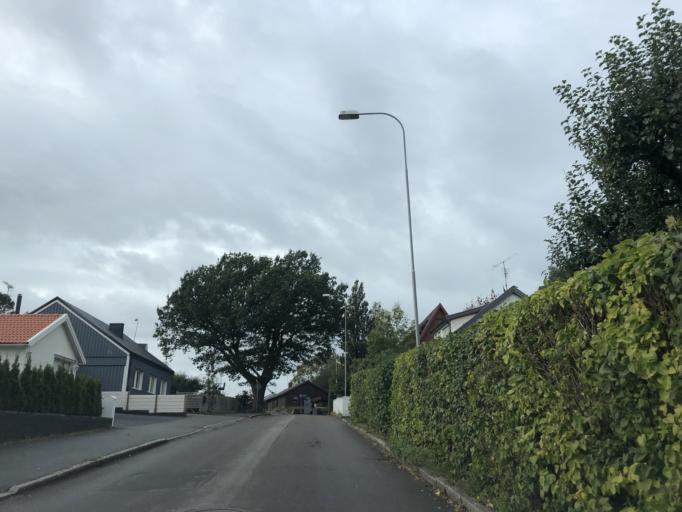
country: SE
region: Vaestra Goetaland
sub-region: Goteborg
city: Majorna
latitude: 57.6720
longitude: 11.8676
